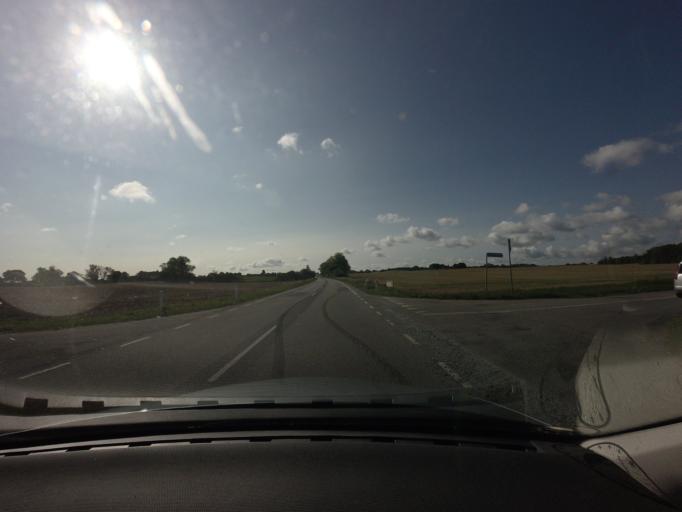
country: DK
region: Zealand
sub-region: Vordingborg Kommune
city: Praesto
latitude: 55.0235
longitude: 12.1030
